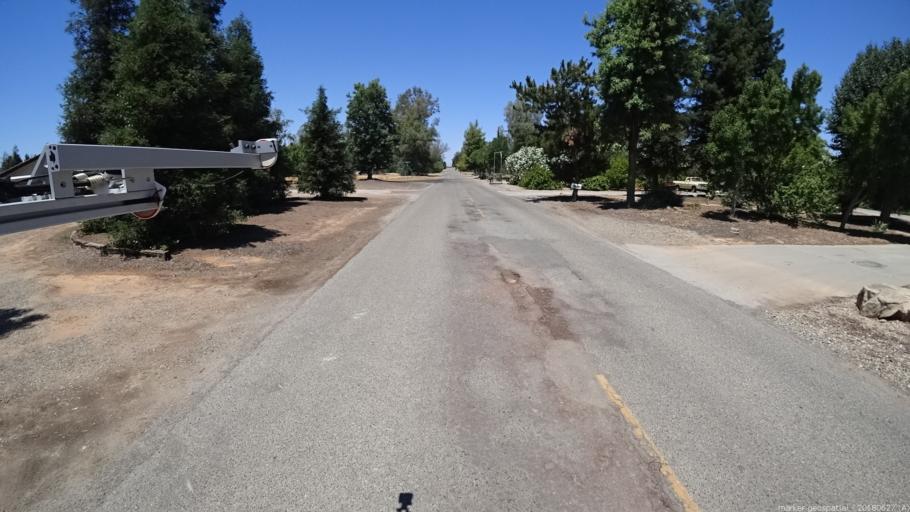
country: US
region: California
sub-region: Madera County
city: Bonadelle Ranchos-Madera Ranchos
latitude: 36.9302
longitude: -119.8710
